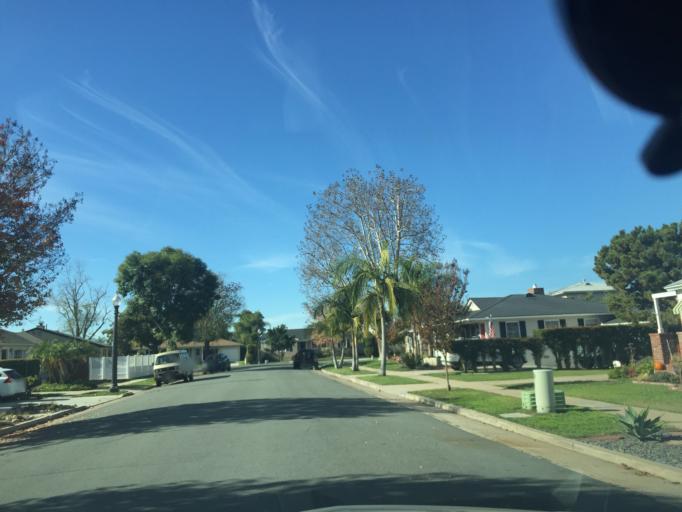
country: US
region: California
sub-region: San Diego County
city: Lemon Grove
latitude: 32.7658
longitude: -117.0872
